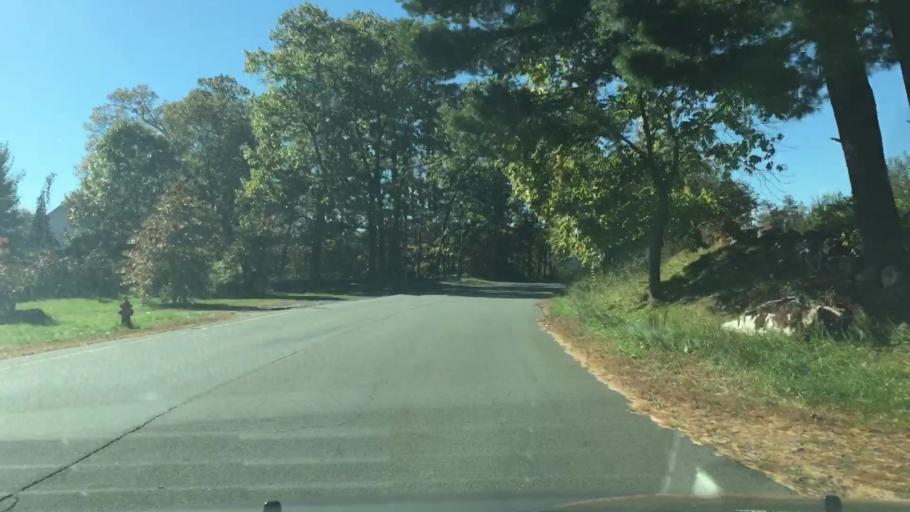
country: US
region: Massachusetts
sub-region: Essex County
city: North Andover
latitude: 42.6896
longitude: -71.0713
